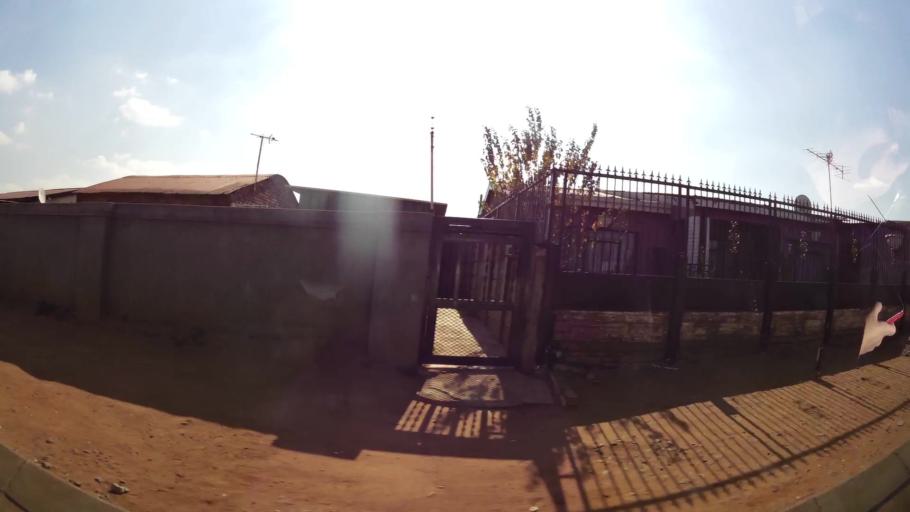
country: ZA
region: Gauteng
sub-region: Ekurhuleni Metropolitan Municipality
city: Brakpan
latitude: -26.1523
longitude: 28.4118
